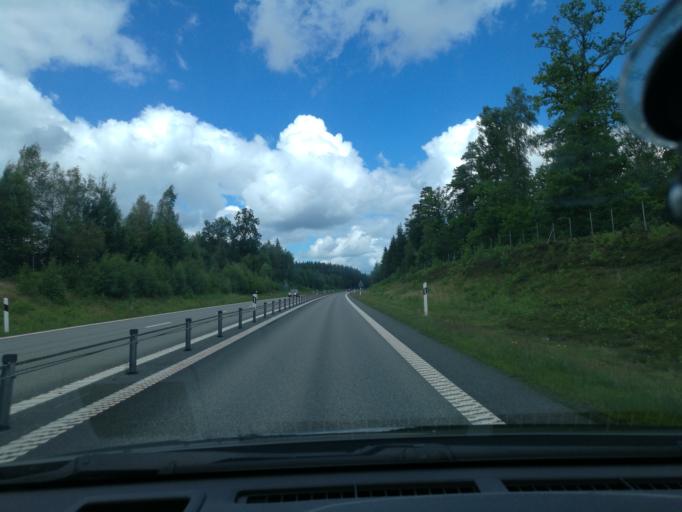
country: SE
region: Skane
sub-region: Hassleholms Kommun
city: Hassleholm
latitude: 56.1892
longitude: 13.8468
